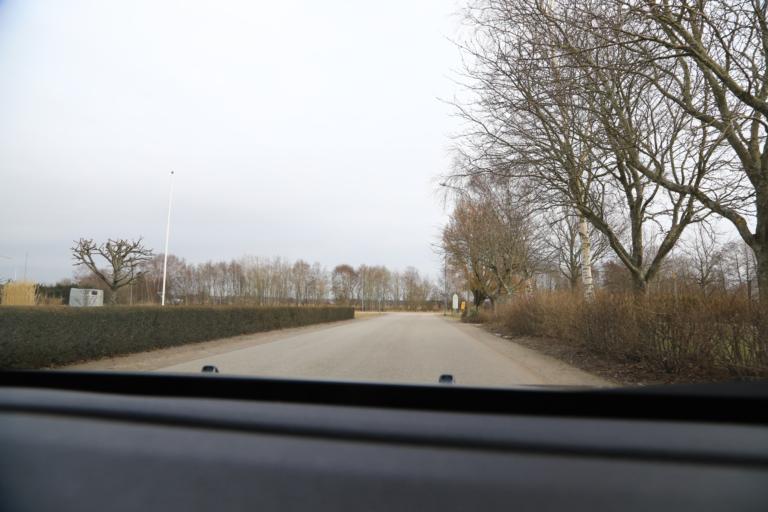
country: SE
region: Halland
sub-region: Kungsbacka Kommun
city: Frillesas
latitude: 57.2385
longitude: 12.1314
